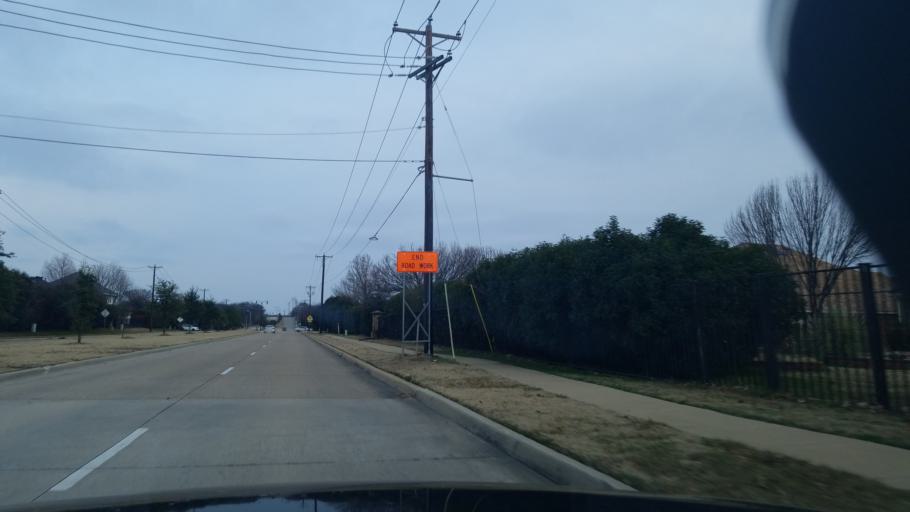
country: US
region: Texas
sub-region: Denton County
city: Corinth
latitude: 33.1422
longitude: -97.0854
